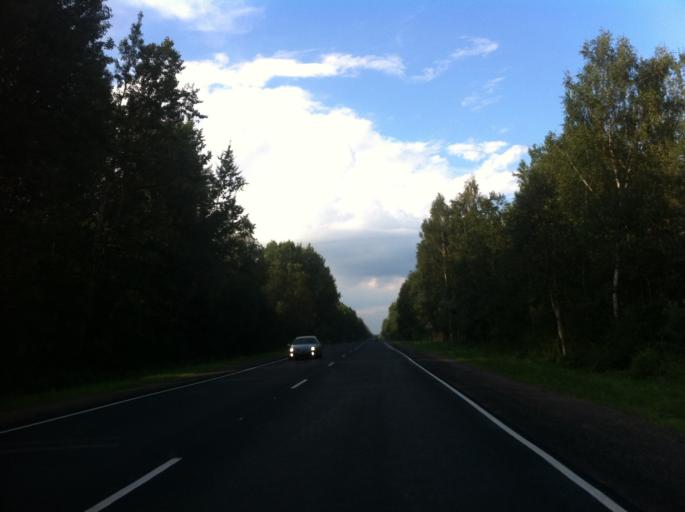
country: RU
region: Leningrad
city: Luga
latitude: 58.4905
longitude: 29.7813
